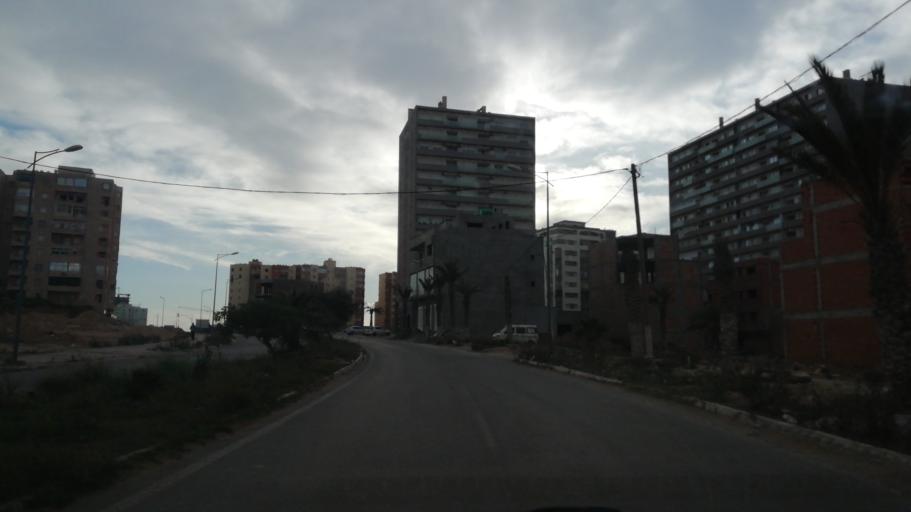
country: DZ
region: Oran
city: Bir el Djir
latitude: 35.7118
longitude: -0.5646
